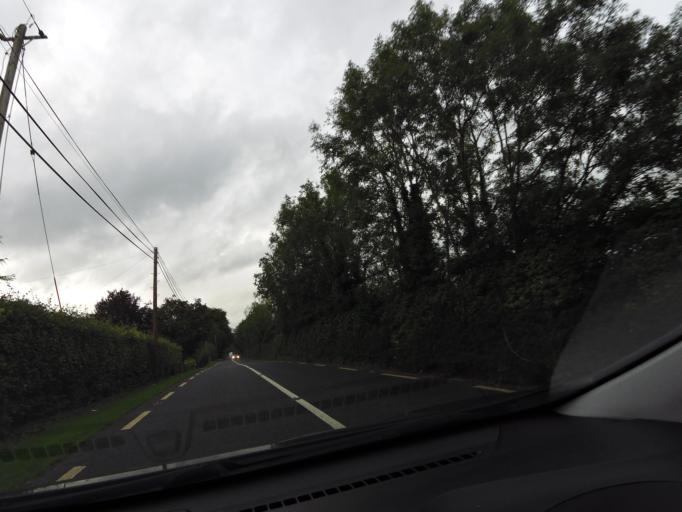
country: IE
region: Leinster
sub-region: An Iarmhi
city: Athlone
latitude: 53.3926
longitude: -7.8708
